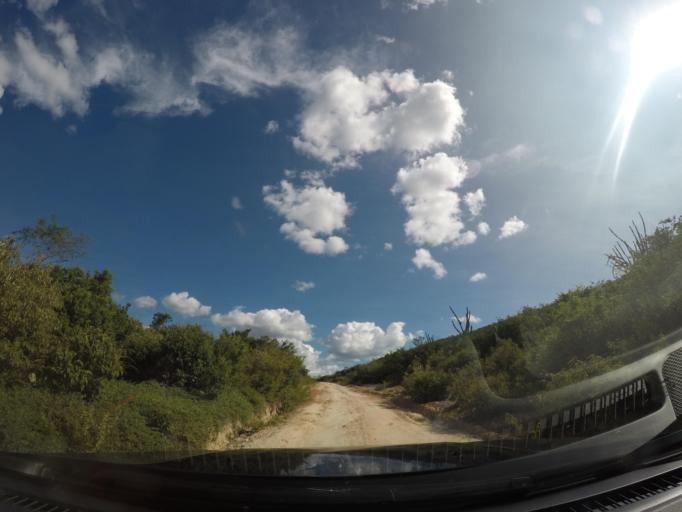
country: BR
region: Bahia
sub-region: Barra Da Estiva
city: Barra da Estiva
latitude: -13.2009
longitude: -41.5947
